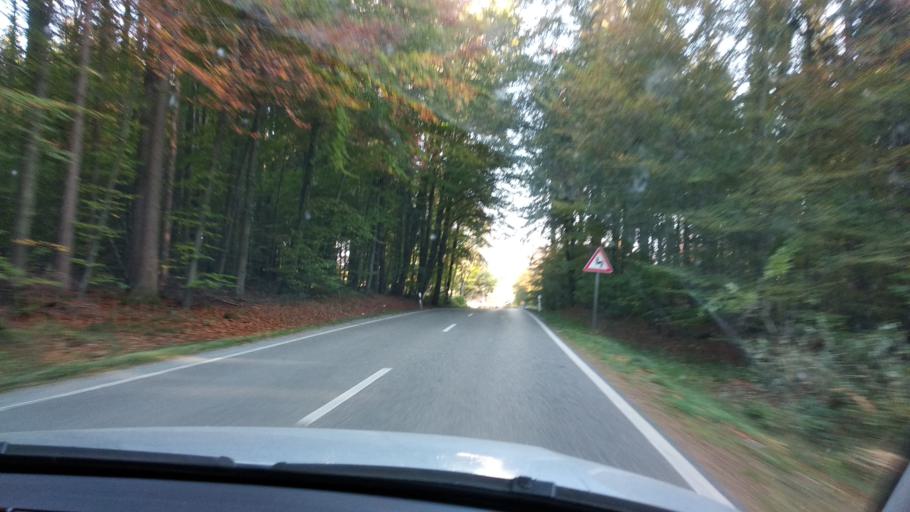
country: DE
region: Bavaria
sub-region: Upper Bavaria
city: Oberpframmern
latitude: 47.9974
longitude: 11.8260
